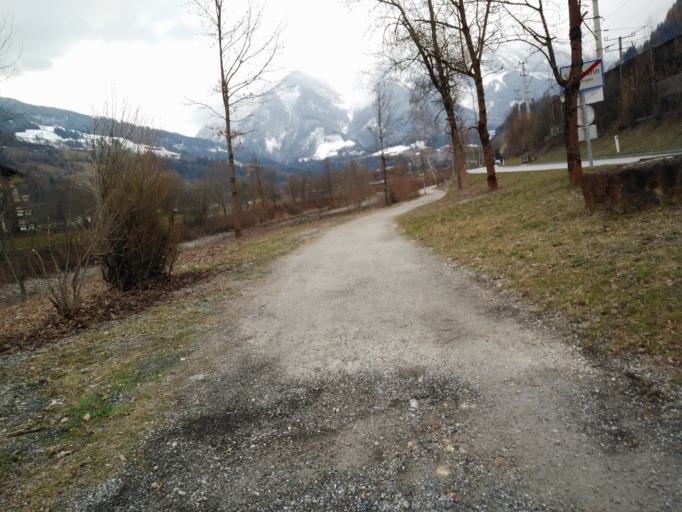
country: AT
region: Salzburg
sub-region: Politischer Bezirk Sankt Johann im Pongau
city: Sankt Johann im Pongau
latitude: 47.3439
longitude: 13.1948
